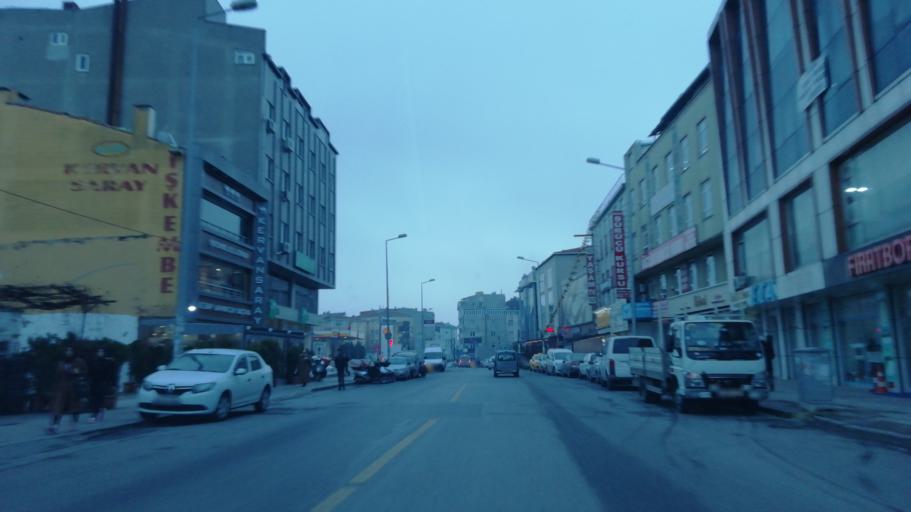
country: TR
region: Istanbul
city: Bahcelievler
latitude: 41.0104
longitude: 28.8298
